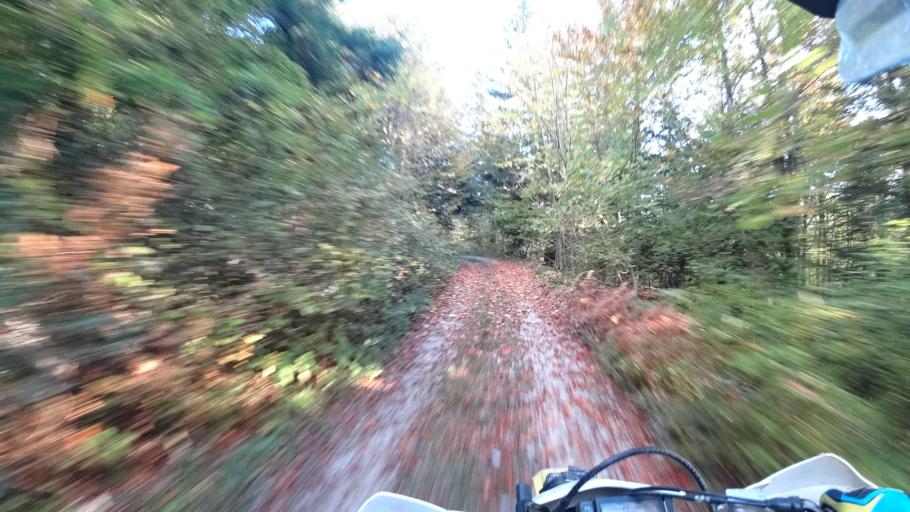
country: HR
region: Karlovacka
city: Plaski
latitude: 45.0093
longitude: 15.4301
